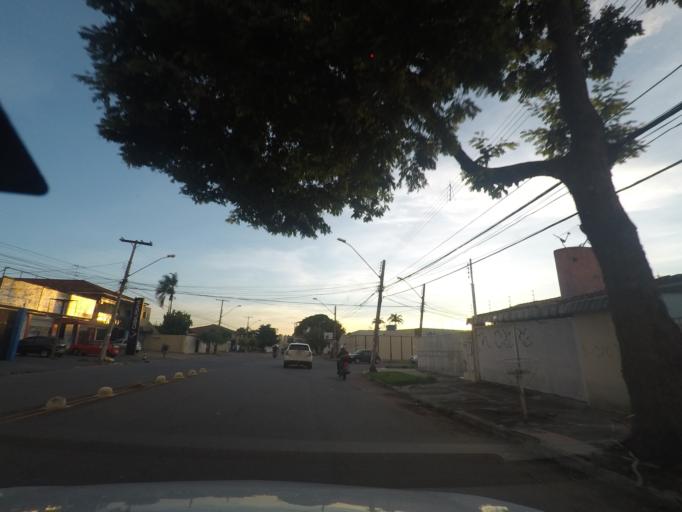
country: BR
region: Goias
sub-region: Goiania
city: Goiania
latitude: -16.6902
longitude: -49.2837
